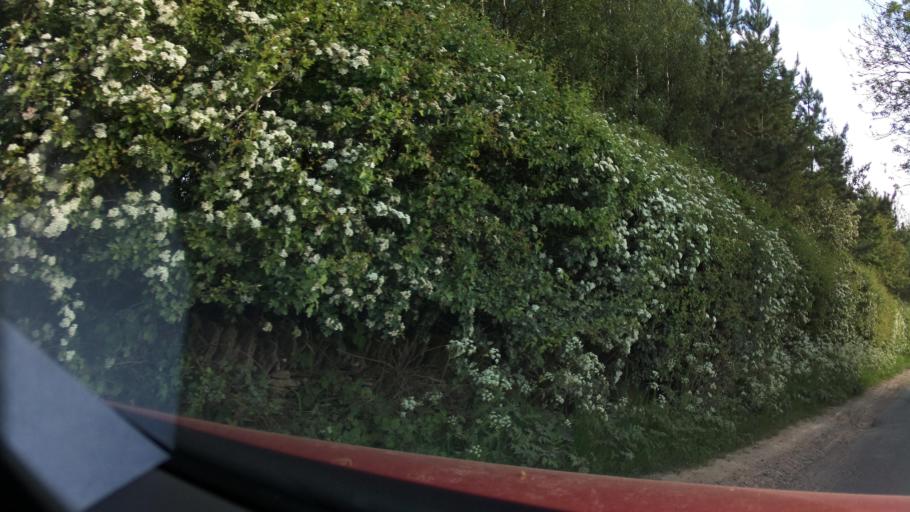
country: GB
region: England
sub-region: Gloucestershire
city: Westfield
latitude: 51.9301
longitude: -1.8295
